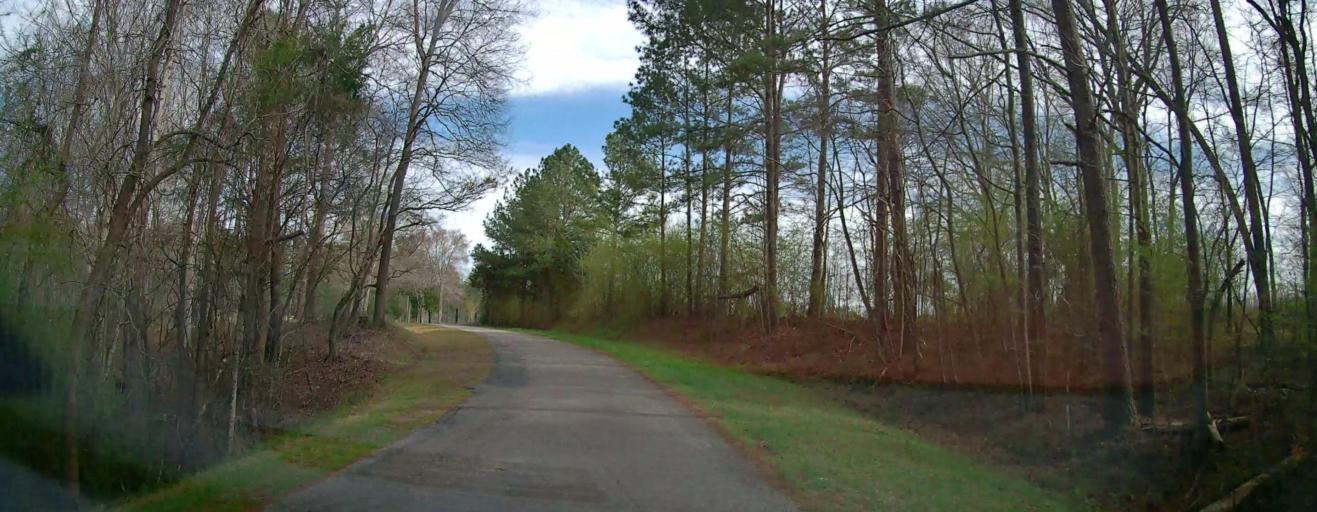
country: US
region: Georgia
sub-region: Monroe County
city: Forsyth
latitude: 33.0404
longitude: -83.8905
